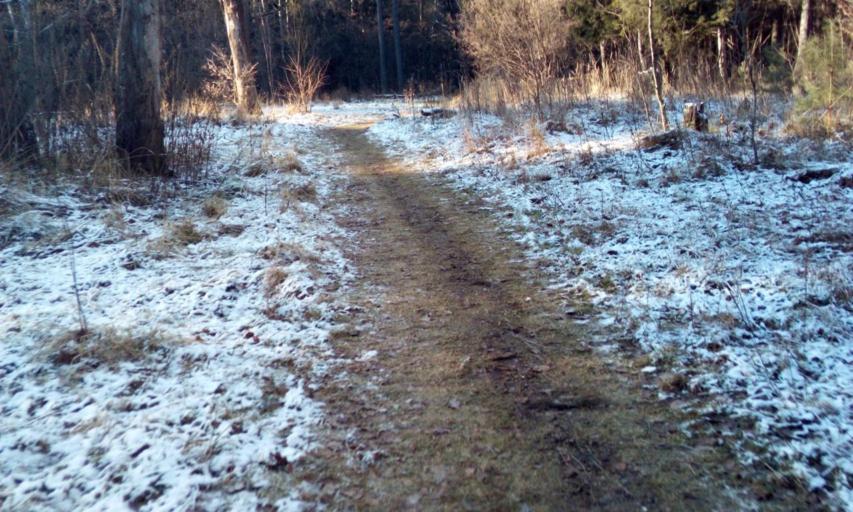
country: RU
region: Moskovskaya
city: Aprelevka
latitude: 55.5466
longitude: 37.0921
